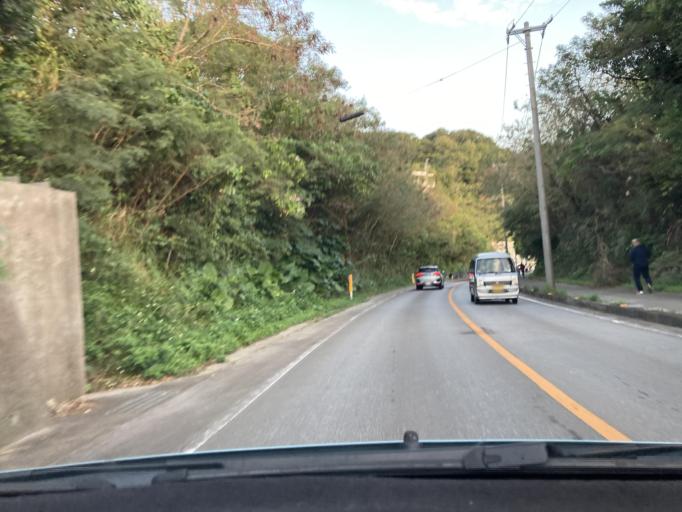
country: JP
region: Okinawa
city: Ginowan
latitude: 26.1682
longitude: 127.8170
